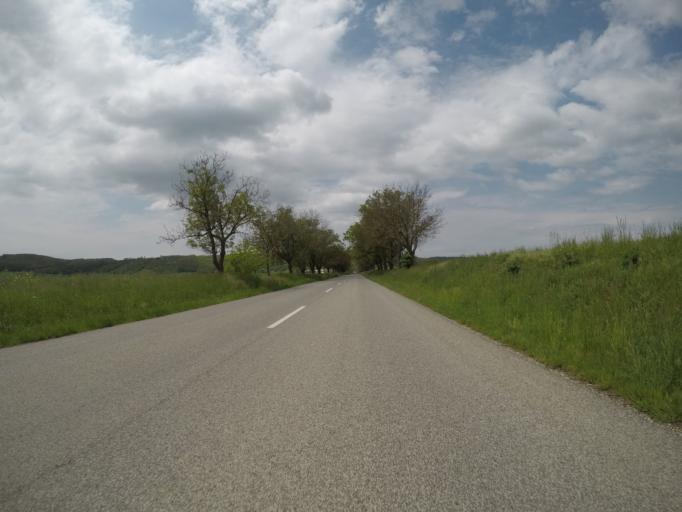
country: SK
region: Banskobystricky
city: Dudince
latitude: 48.0803
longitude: 18.8131
